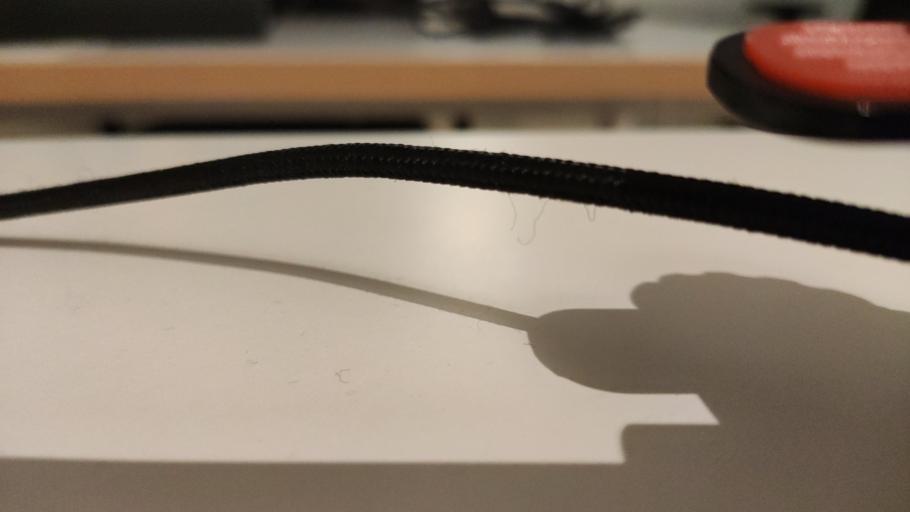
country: RU
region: Moskovskaya
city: Dmitrov
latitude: 56.3572
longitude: 37.4931
